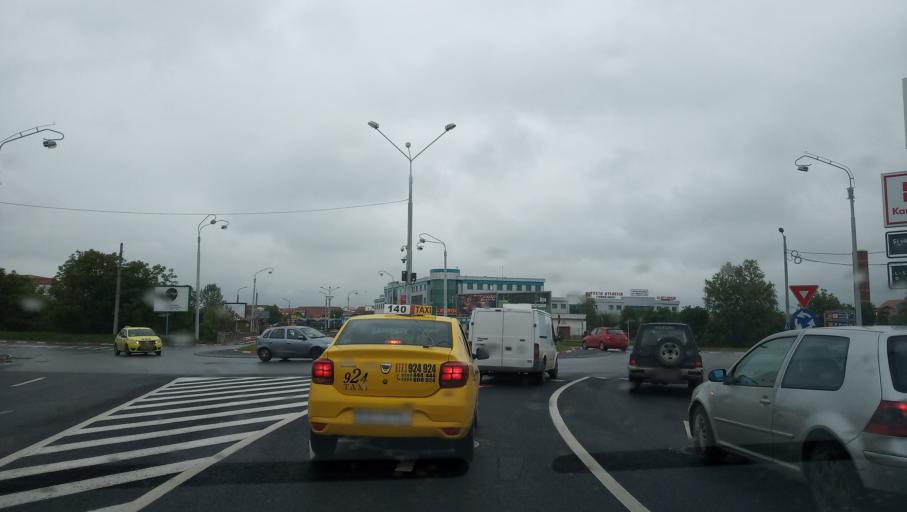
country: RO
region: Sibiu
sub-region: Municipiul Sibiu
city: Sibiu
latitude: 45.7930
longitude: 24.1333
